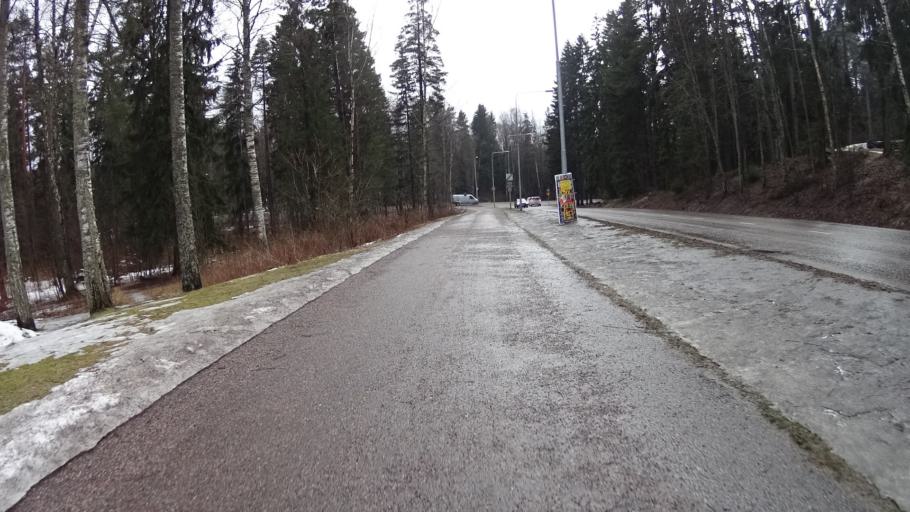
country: FI
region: Uusimaa
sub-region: Helsinki
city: Kilo
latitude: 60.2028
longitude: 24.7981
